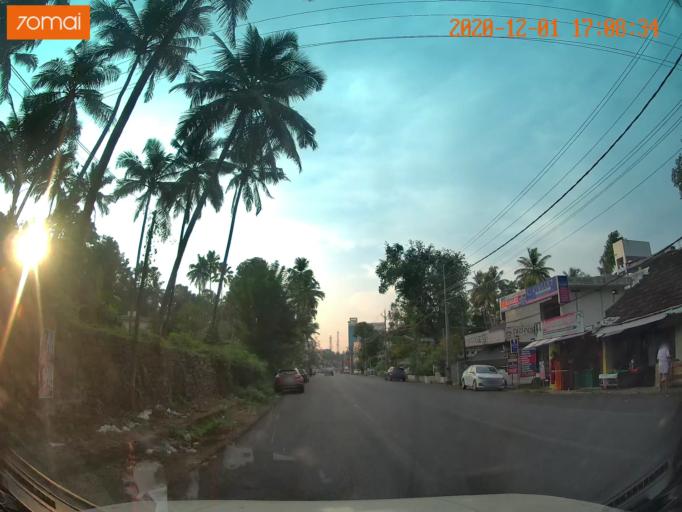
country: IN
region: Kerala
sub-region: Ernakulam
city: Muvattupula
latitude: 9.9782
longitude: 76.5886
